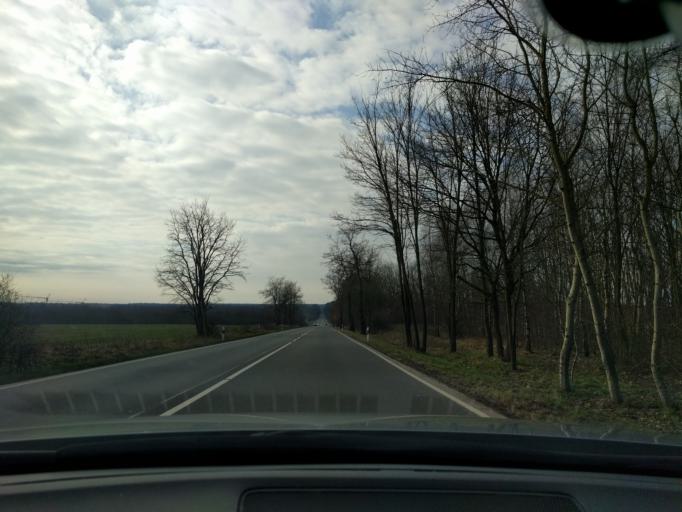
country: DE
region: Saxony-Anhalt
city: Colbitz
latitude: 52.3883
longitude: 11.6194
